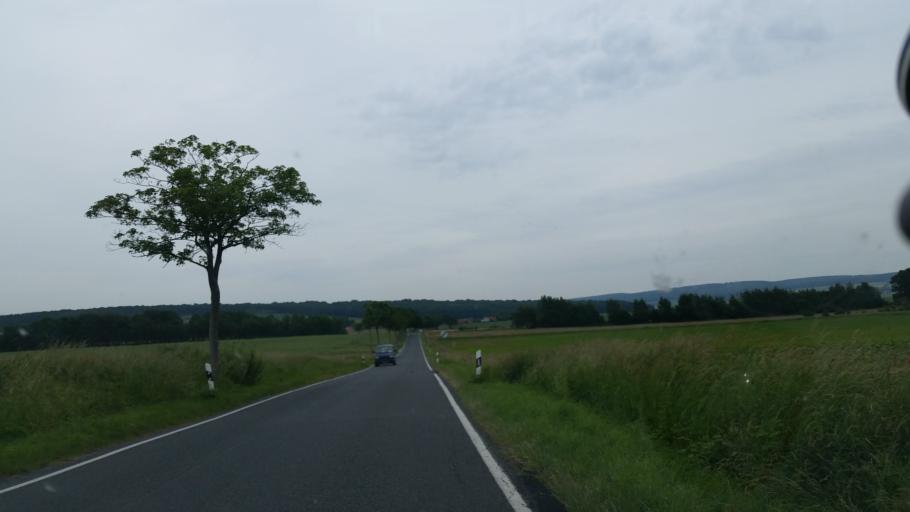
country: DE
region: Lower Saxony
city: Erkerode
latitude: 52.2946
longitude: 10.7377
